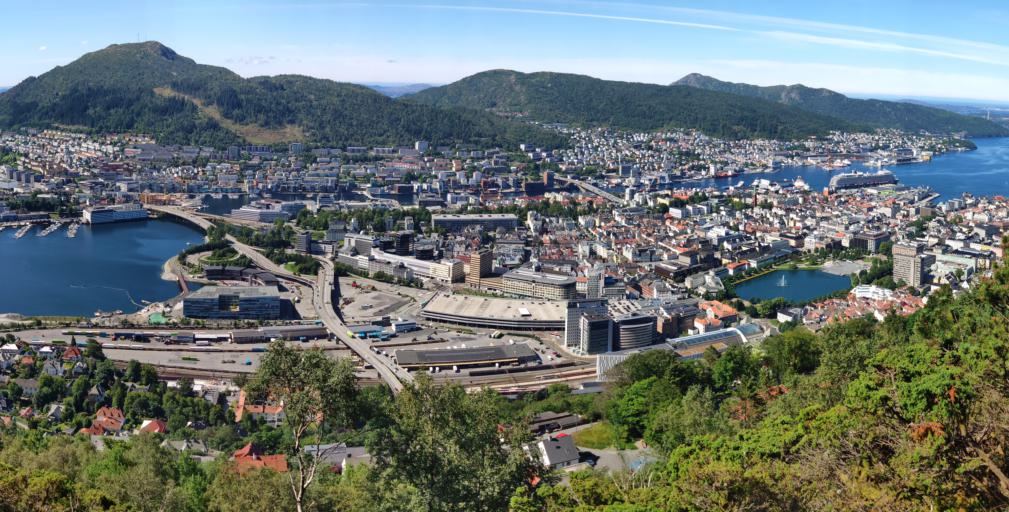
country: NO
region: Hordaland
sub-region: Bergen
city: Bergen
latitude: 60.3921
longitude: 5.3468
